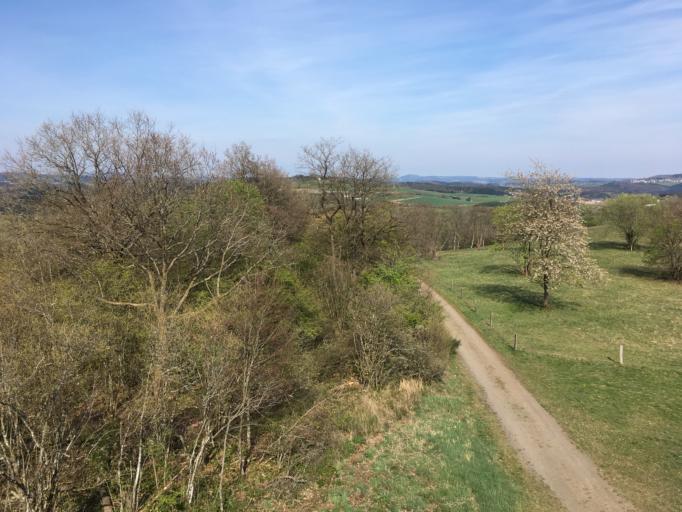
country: DE
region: Rheinland-Pfalz
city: Schalkenmehren
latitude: 50.1756
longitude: 6.8422
